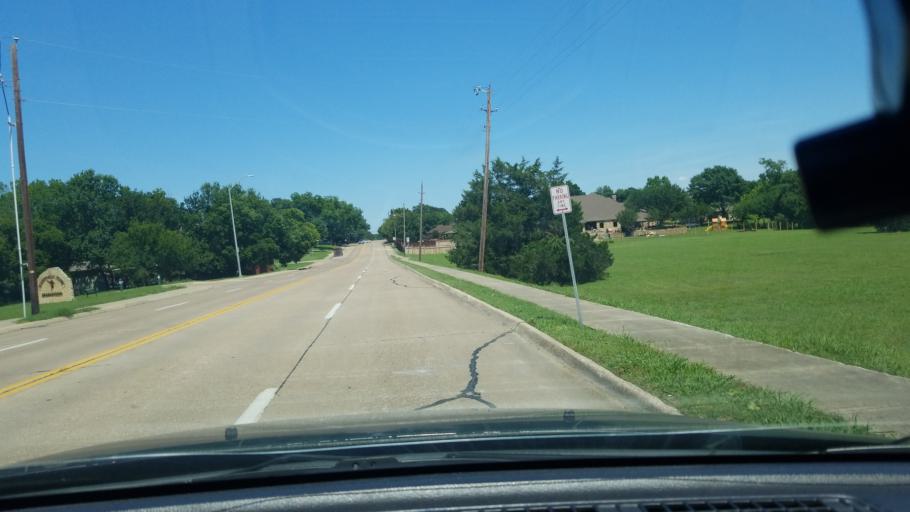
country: US
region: Texas
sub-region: Dallas County
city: Mesquite
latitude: 32.7558
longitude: -96.6088
